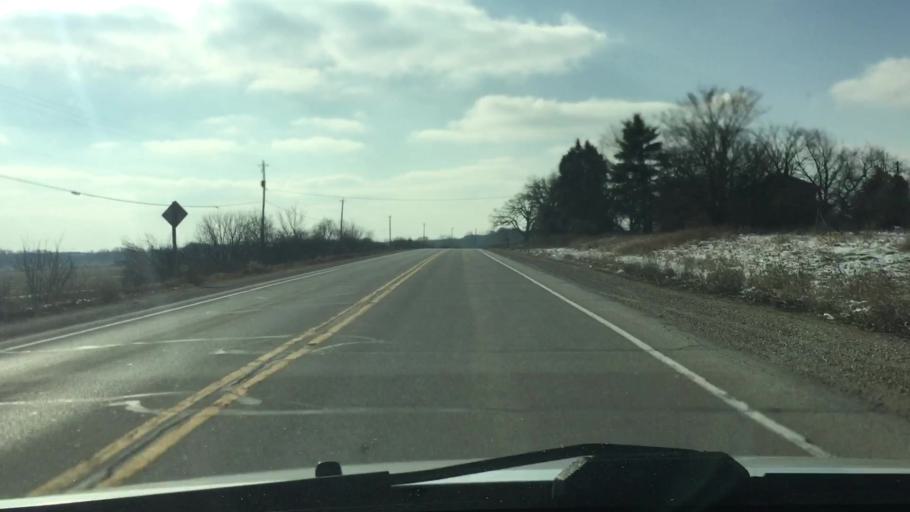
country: US
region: Wisconsin
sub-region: Waukesha County
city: North Prairie
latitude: 42.9269
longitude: -88.4283
